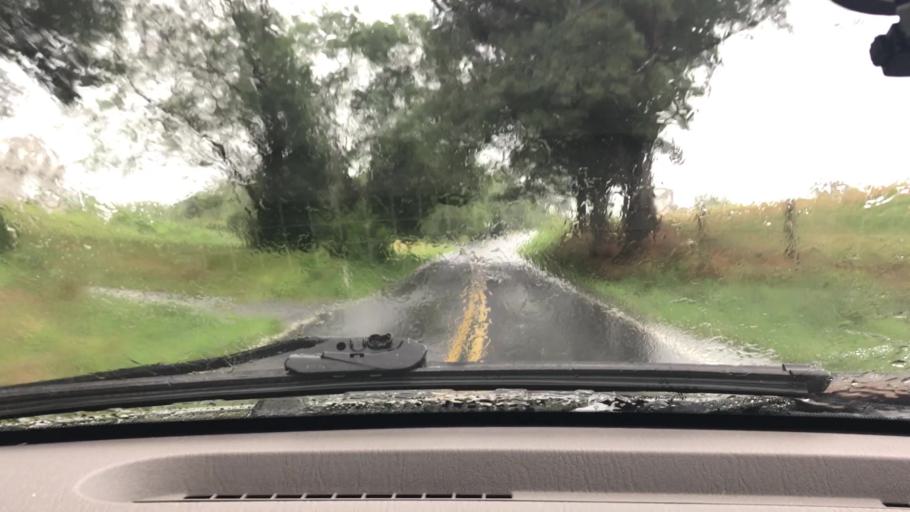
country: US
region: Pennsylvania
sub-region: Lancaster County
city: Elizabethtown
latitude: 40.1251
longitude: -76.6096
